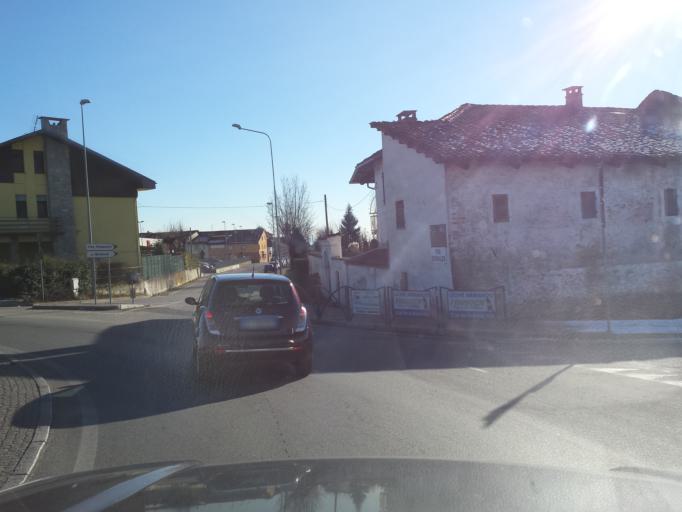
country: IT
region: Piedmont
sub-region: Provincia di Torino
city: Rivarolo Canavese
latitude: 45.3205
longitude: 7.7293
